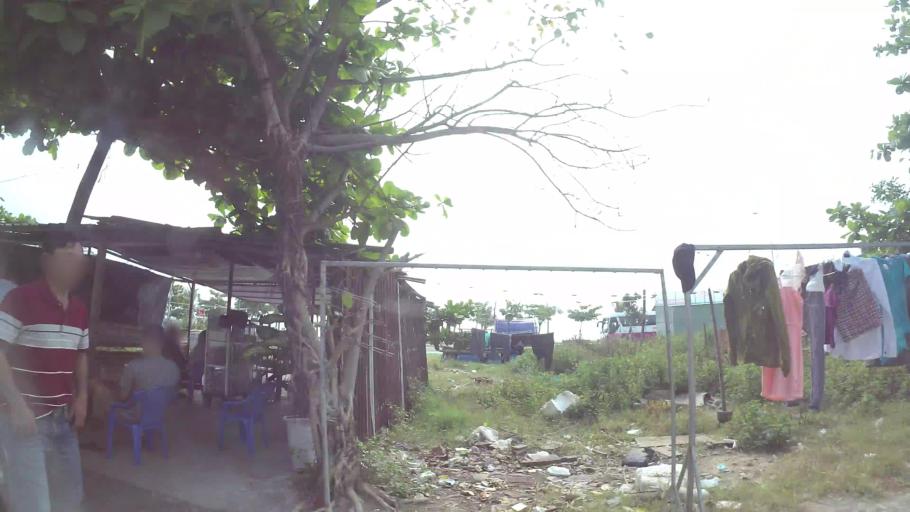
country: VN
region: Da Nang
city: Son Tra
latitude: 16.0927
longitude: 108.2510
